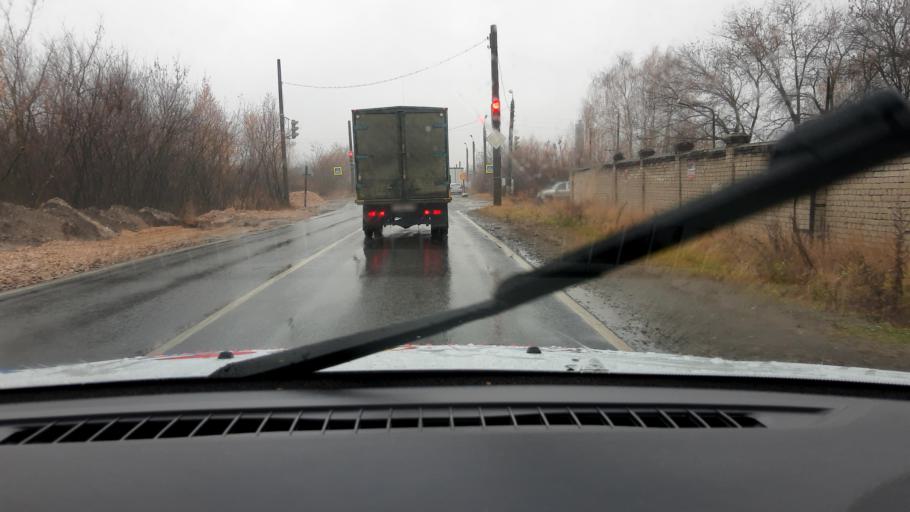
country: RU
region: Nizjnij Novgorod
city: Babino
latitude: 56.2584
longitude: 43.6376
